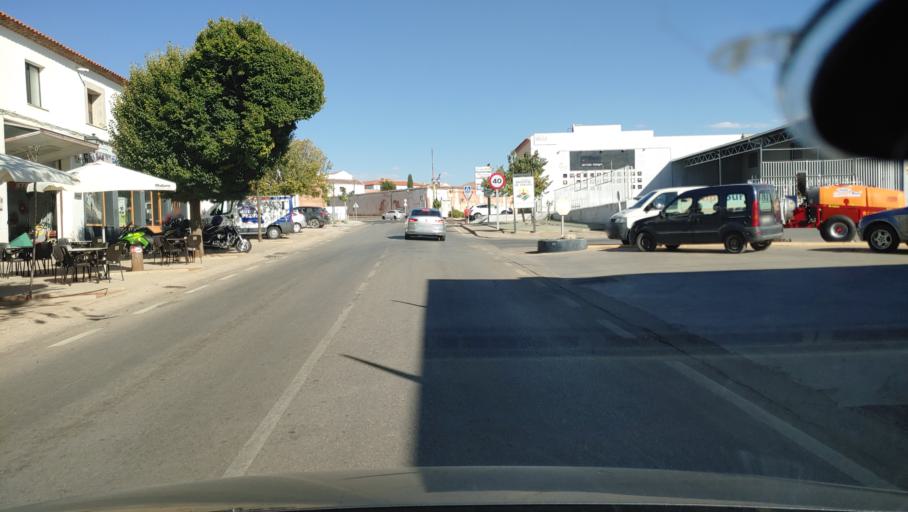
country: ES
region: Castille-La Mancha
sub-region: Provincia de Ciudad Real
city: Infantes
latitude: 38.7369
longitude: -3.0195
